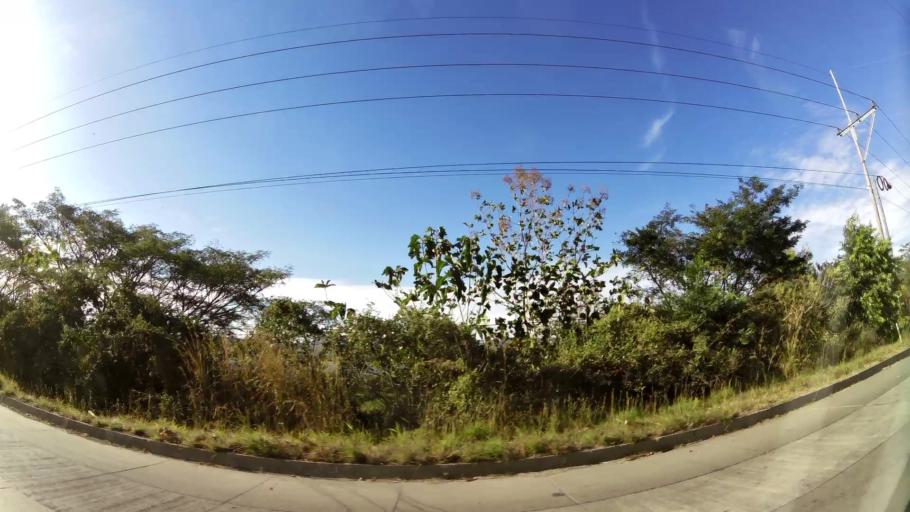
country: SV
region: Santa Ana
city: Metapan
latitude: 14.3050
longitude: -89.4548
